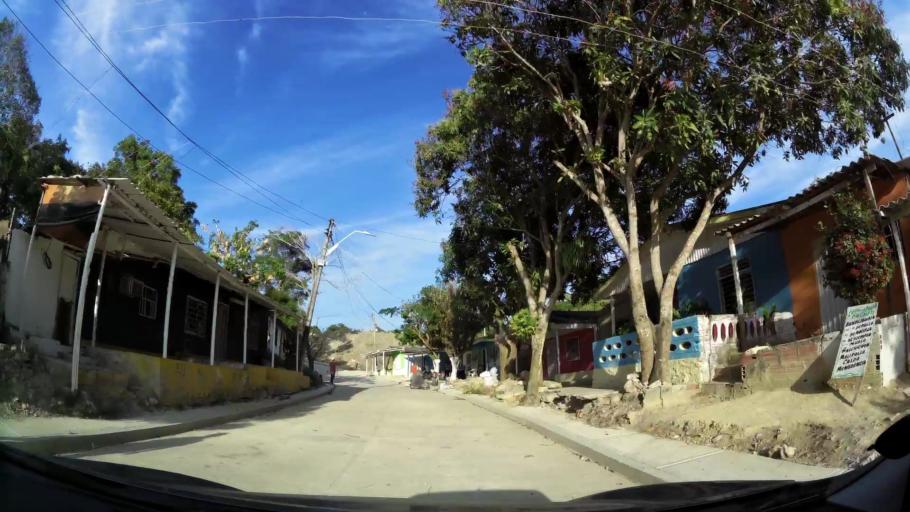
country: CO
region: Atlantico
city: Barranquilla
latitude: 10.9556
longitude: -74.8119
